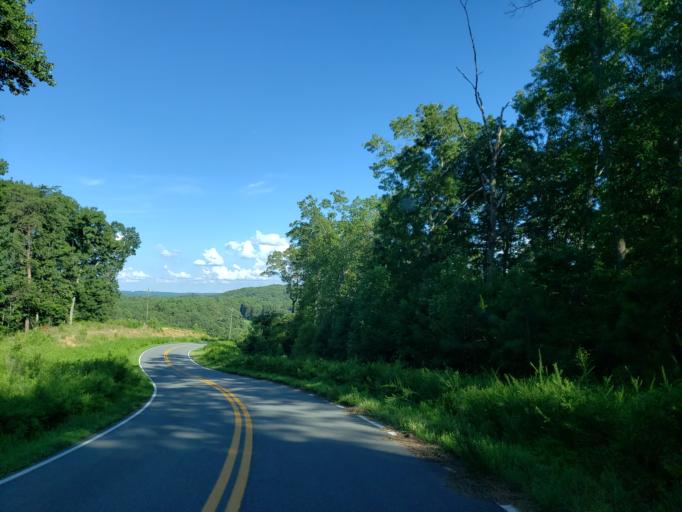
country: US
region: Georgia
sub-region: Bartow County
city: Rydal
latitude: 34.3532
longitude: -84.6017
